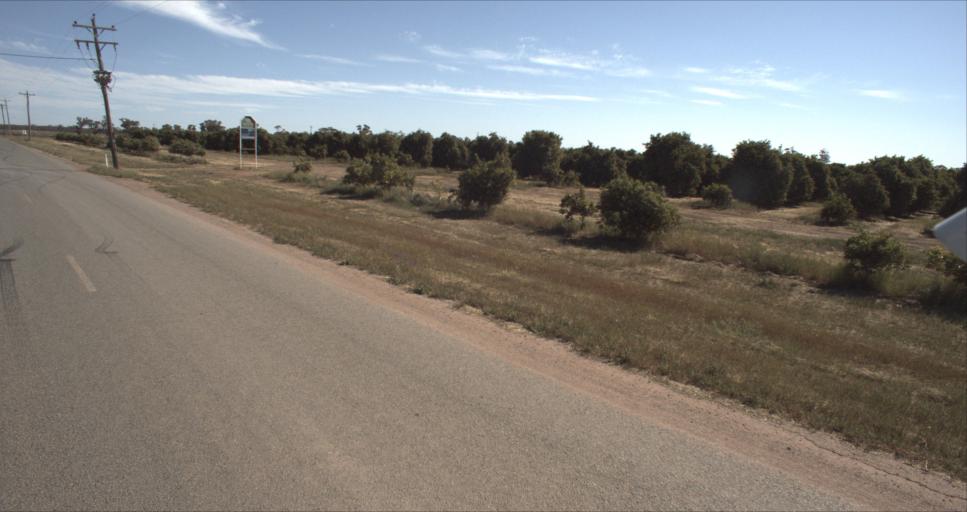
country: AU
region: New South Wales
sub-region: Leeton
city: Leeton
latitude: -34.5858
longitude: 146.3790
